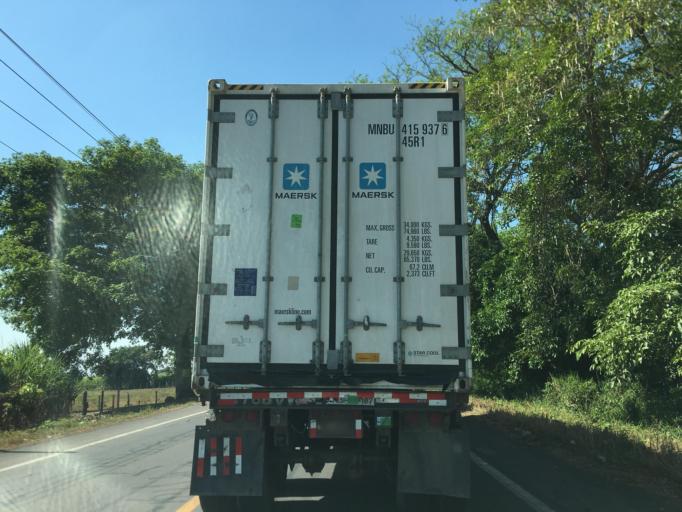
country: GT
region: Escuintla
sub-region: Municipio de Masagua
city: Masagua
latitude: 14.1914
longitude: -90.8563
